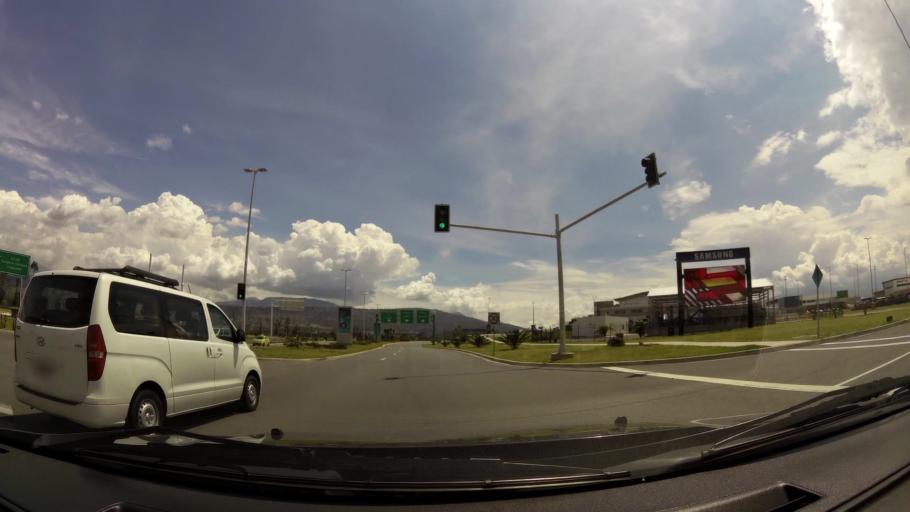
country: EC
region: Pichincha
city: Quito
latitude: -0.1305
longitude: -78.3598
